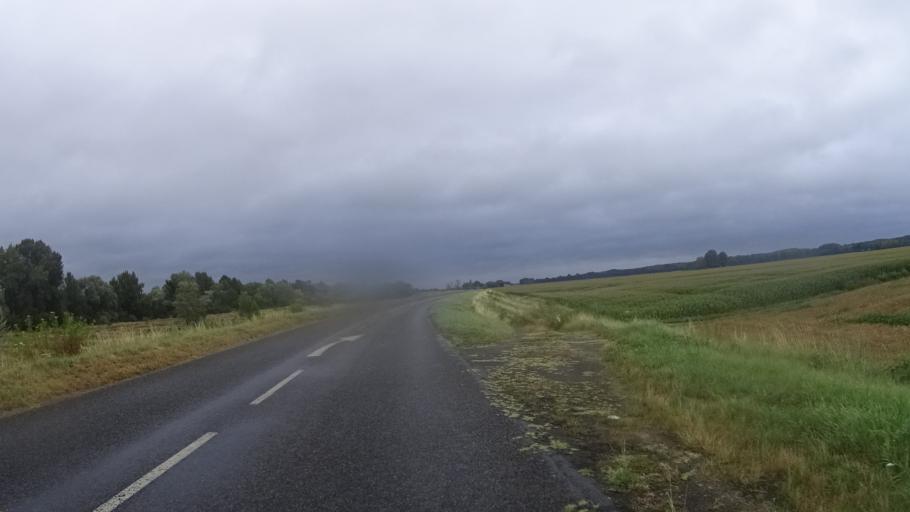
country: FR
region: Centre
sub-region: Departement du Loir-et-Cher
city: Chouzy-sur-Cisse
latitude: 47.5202
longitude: 1.2586
